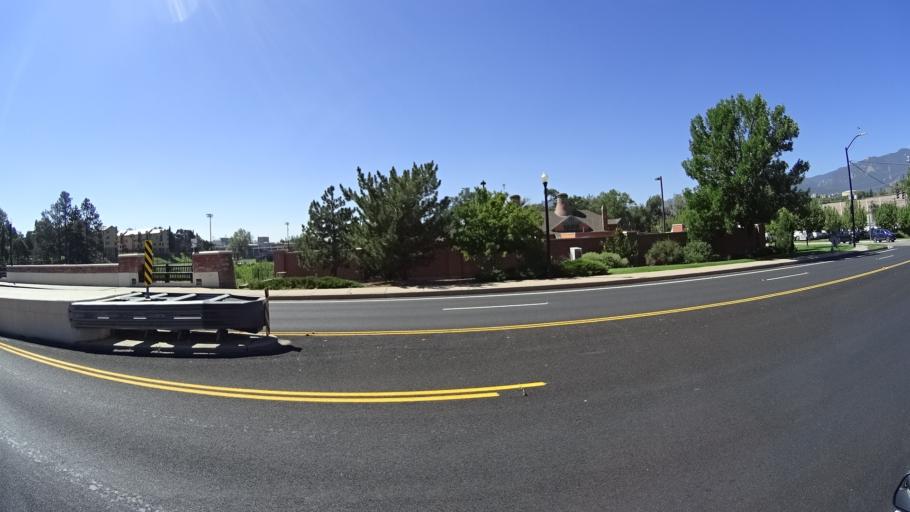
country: US
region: Colorado
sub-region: El Paso County
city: Colorado Springs
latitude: 38.8512
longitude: -104.8293
